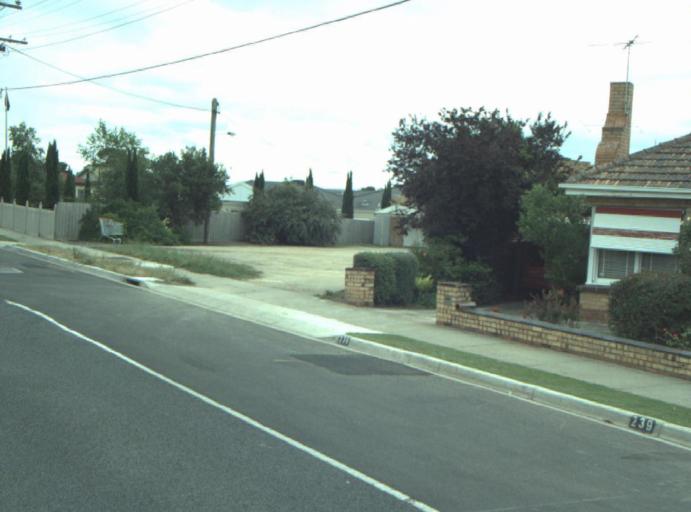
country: AU
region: Victoria
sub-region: Greater Geelong
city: Breakwater
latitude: -38.1782
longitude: 144.3394
